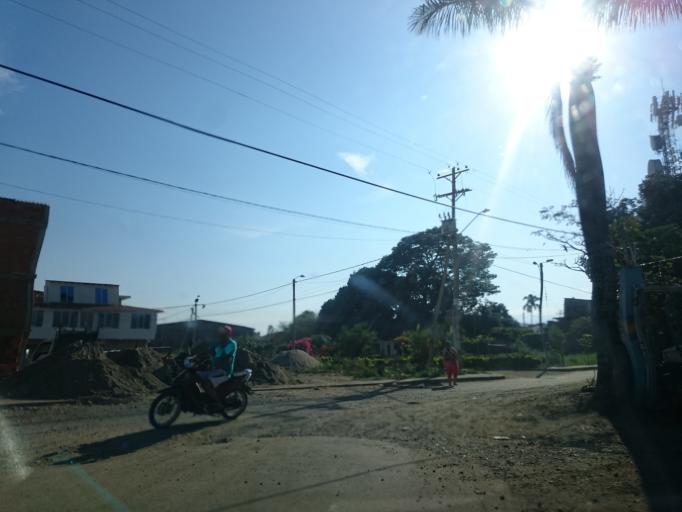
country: CO
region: Cauca
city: Santander de Quilichao
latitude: 3.0103
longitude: -76.4866
